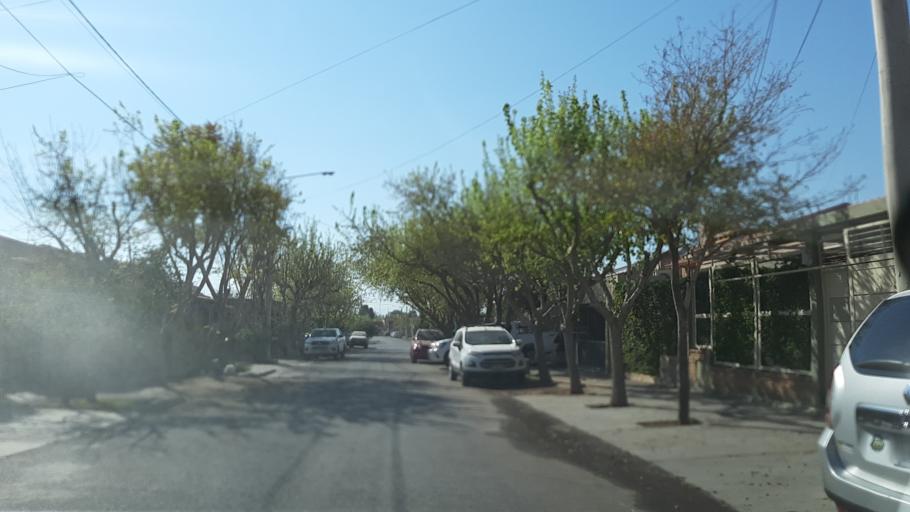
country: AR
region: San Juan
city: San Juan
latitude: -31.5231
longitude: -68.5832
